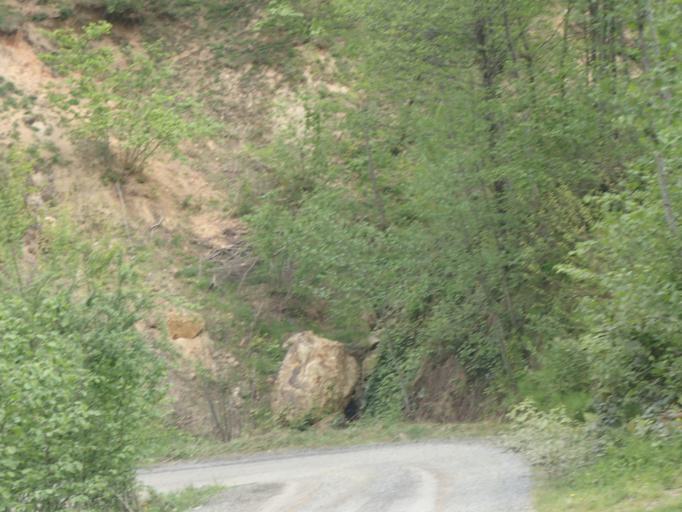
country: TR
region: Ordu
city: Kabaduz
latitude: 40.7964
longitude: 37.9000
